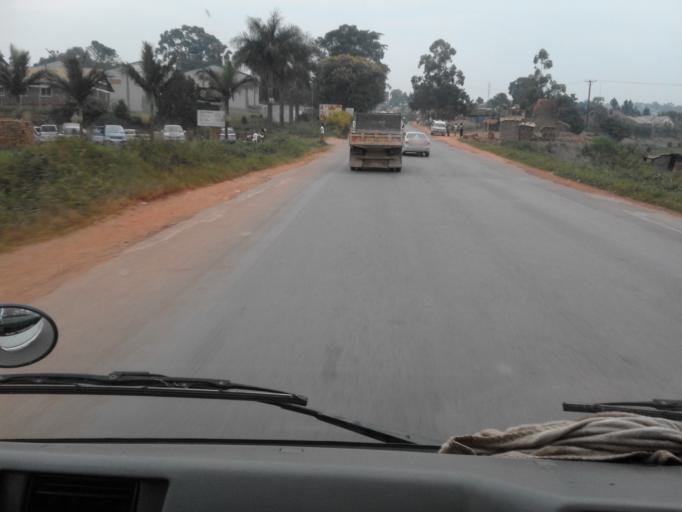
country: UG
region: Central Region
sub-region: Wakiso District
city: Bweyogerere
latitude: 0.3669
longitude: 32.7058
